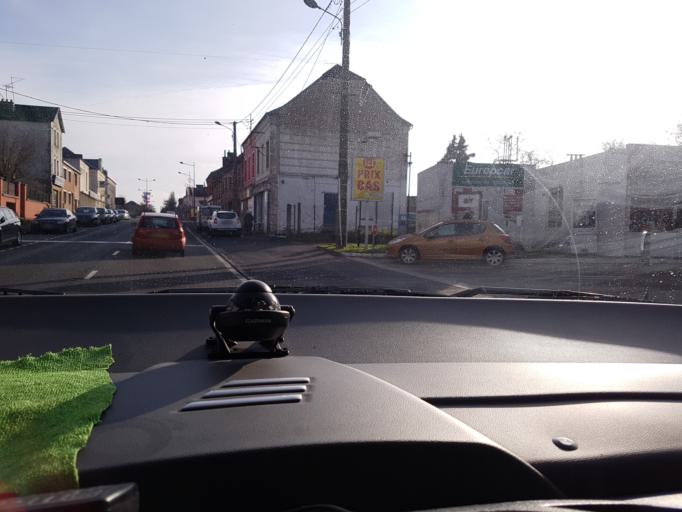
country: FR
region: Picardie
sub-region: Departement de l'Aisne
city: Hirson
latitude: 49.9194
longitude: 4.0845
